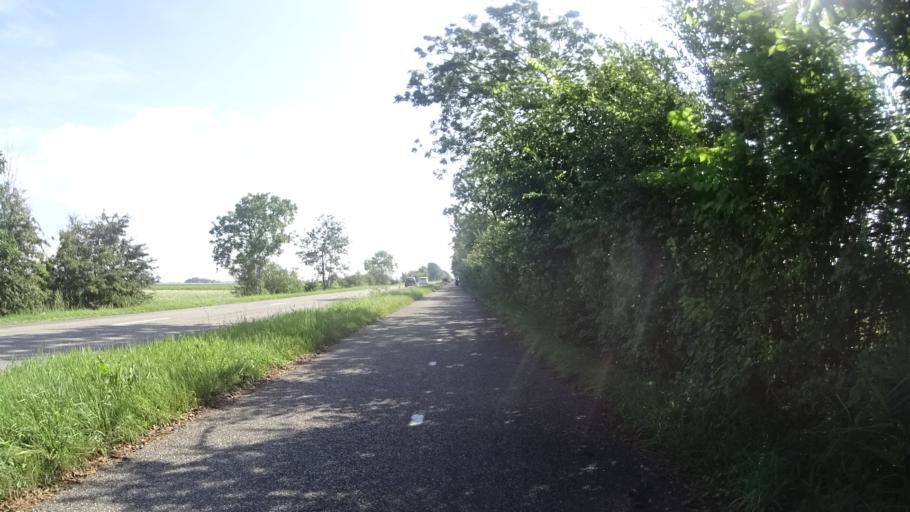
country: NL
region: Friesland
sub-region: Gemeente Franekeradeel
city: Tzum
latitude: 53.1924
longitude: 5.5923
